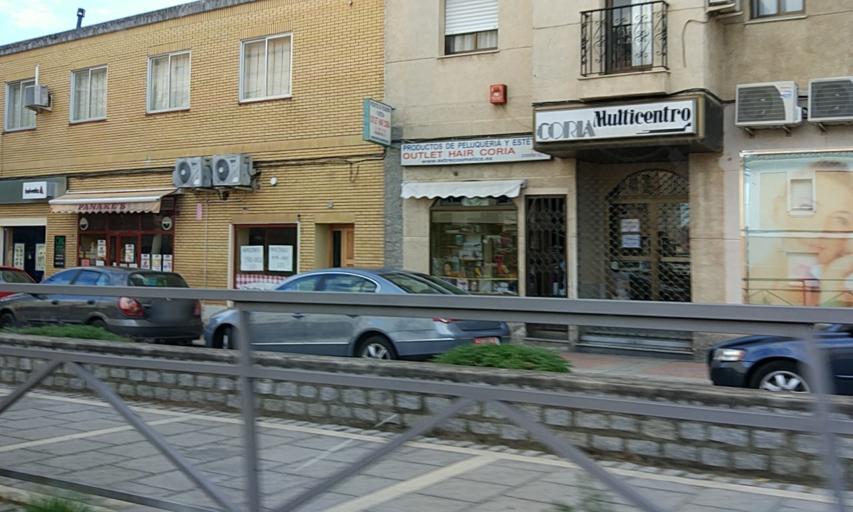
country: ES
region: Extremadura
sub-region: Provincia de Caceres
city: Coria
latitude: 39.9899
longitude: -6.5394
